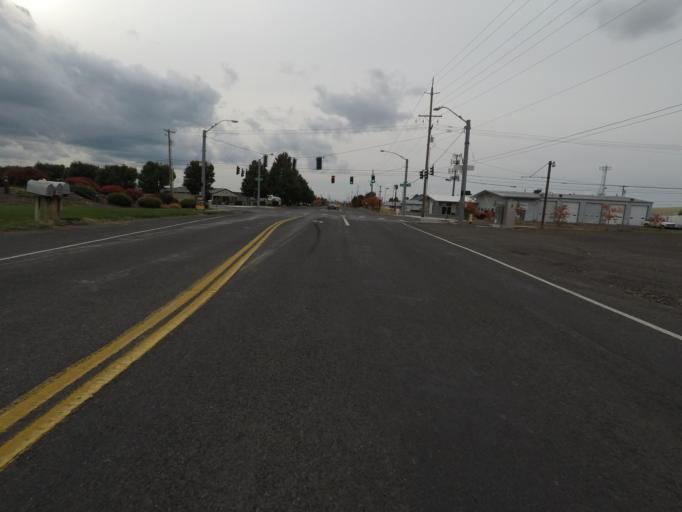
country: US
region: Washington
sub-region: Walla Walla County
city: Walla Walla East
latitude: 46.0804
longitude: -118.2832
